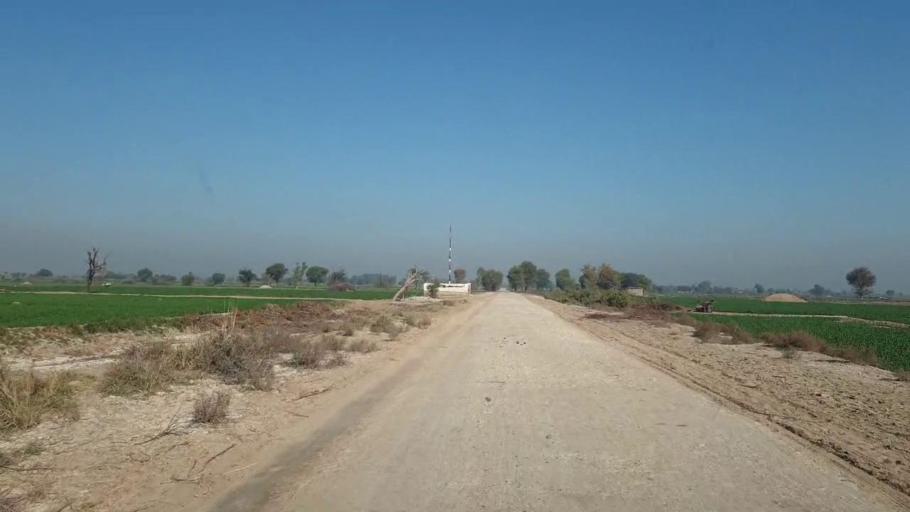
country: PK
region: Sindh
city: Shahdadpur
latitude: 26.0041
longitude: 68.4922
